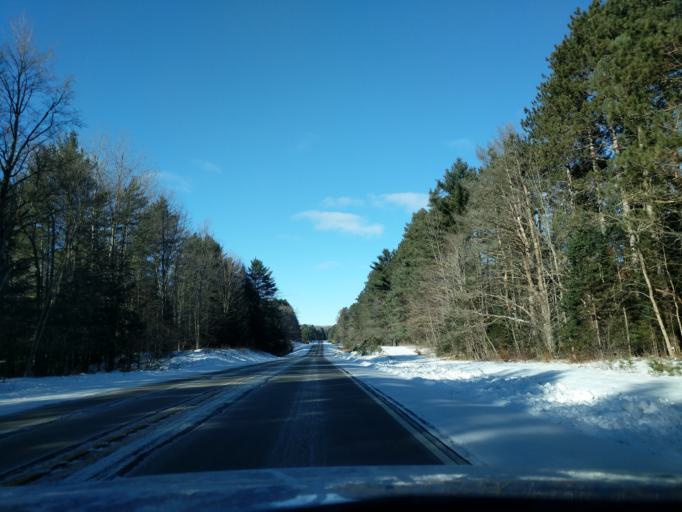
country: US
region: Wisconsin
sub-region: Menominee County
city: Keshena
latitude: 45.1342
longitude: -88.6730
